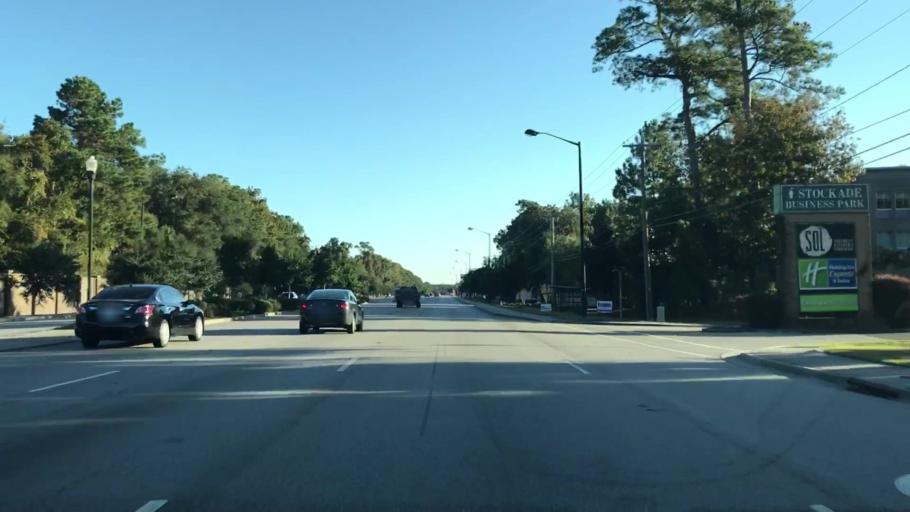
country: US
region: South Carolina
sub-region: Charleston County
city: Isle of Palms
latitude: 32.8369
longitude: -79.8221
